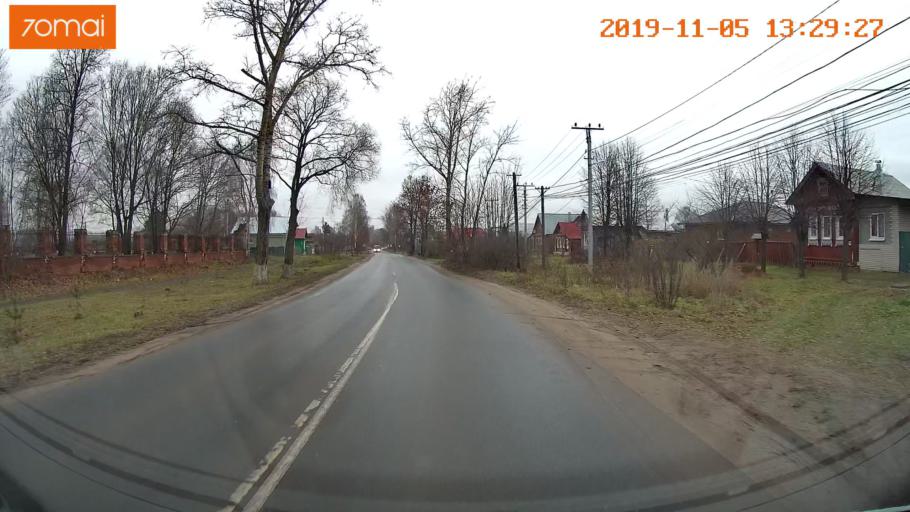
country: RU
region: Ivanovo
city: Shuya
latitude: 56.8607
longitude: 41.3976
